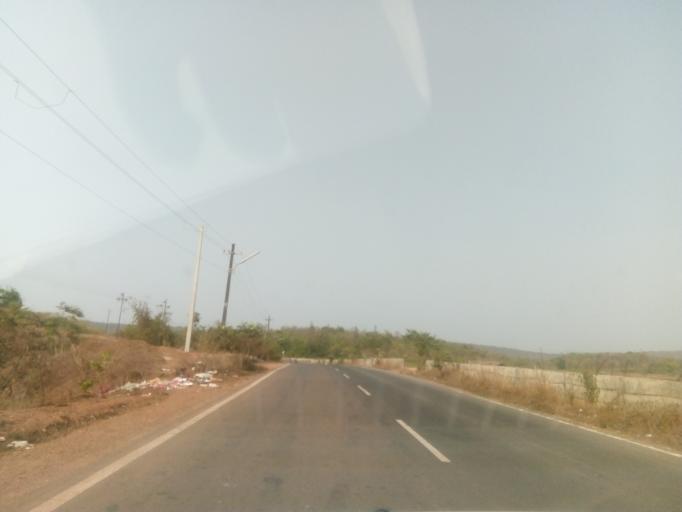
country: IN
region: Goa
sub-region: North Goa
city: Colovale
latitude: 15.6877
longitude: 73.8390
